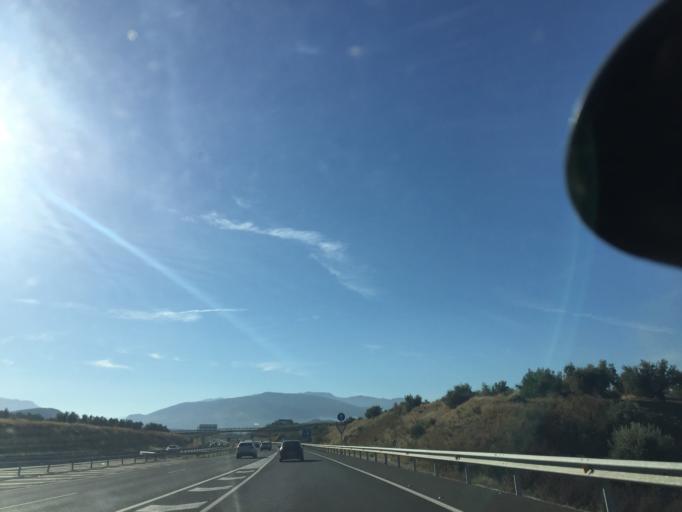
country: ES
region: Andalusia
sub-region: Provincia de Jaen
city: Jaen
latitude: 37.8104
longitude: -3.7644
